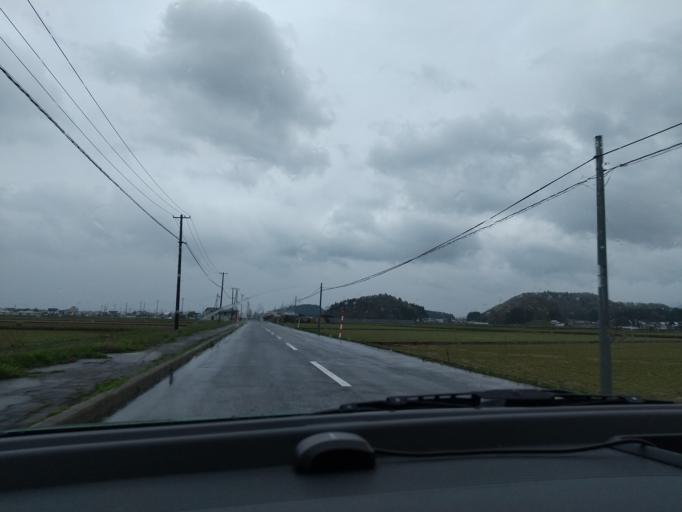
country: JP
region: Akita
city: Yokotemachi
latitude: 39.3582
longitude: 140.5385
